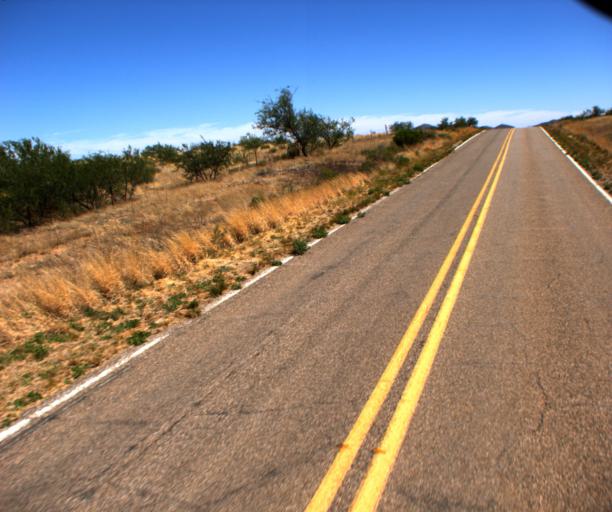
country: US
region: Arizona
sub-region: Santa Cruz County
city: Tubac
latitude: 31.5293
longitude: -111.5414
